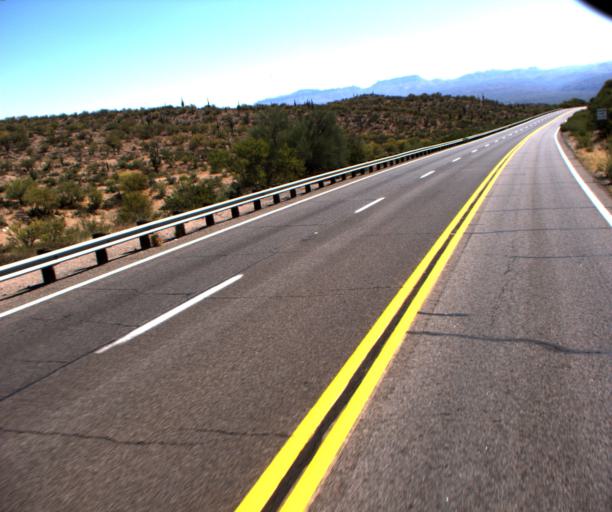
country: US
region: Arizona
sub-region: Pinal County
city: Mammoth
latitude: 32.6692
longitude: -110.6721
